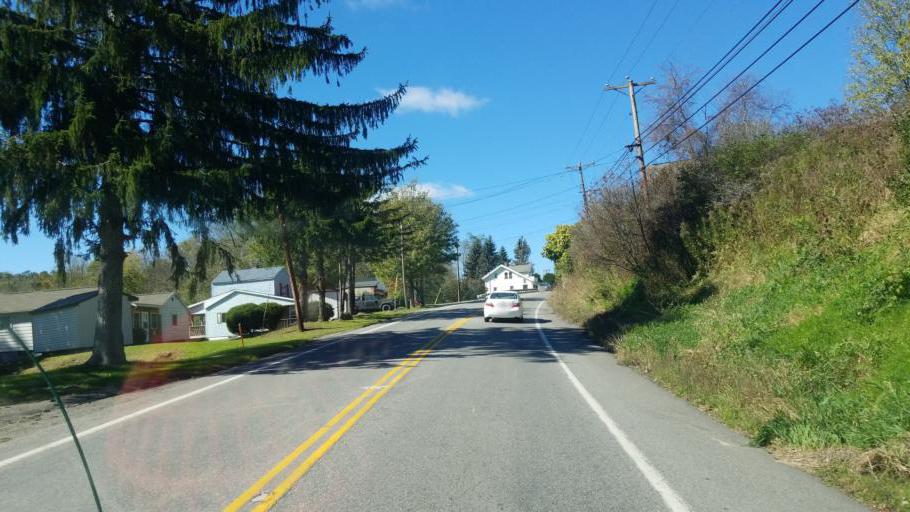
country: US
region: Pennsylvania
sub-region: Somerset County
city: Boswell
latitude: 40.1490
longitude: -79.0466
